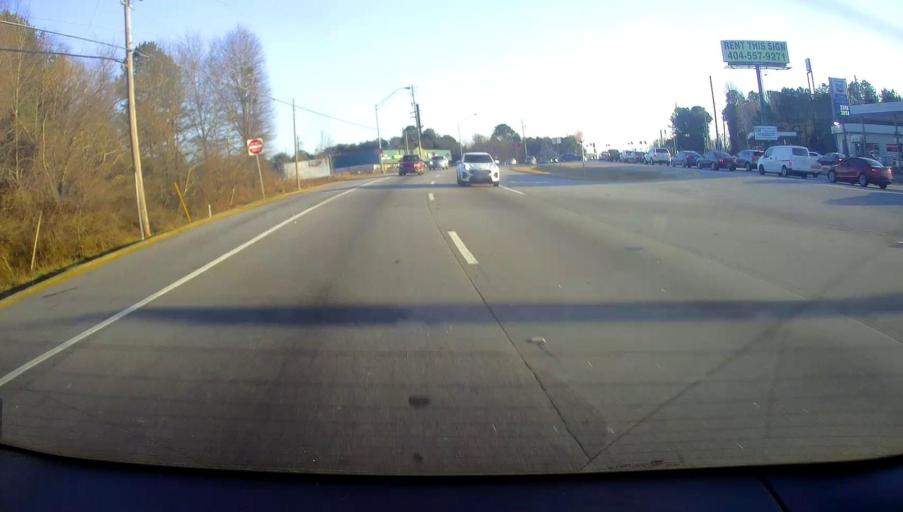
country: US
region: Georgia
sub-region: Fulton County
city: Fairburn
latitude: 33.5490
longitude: -84.5776
